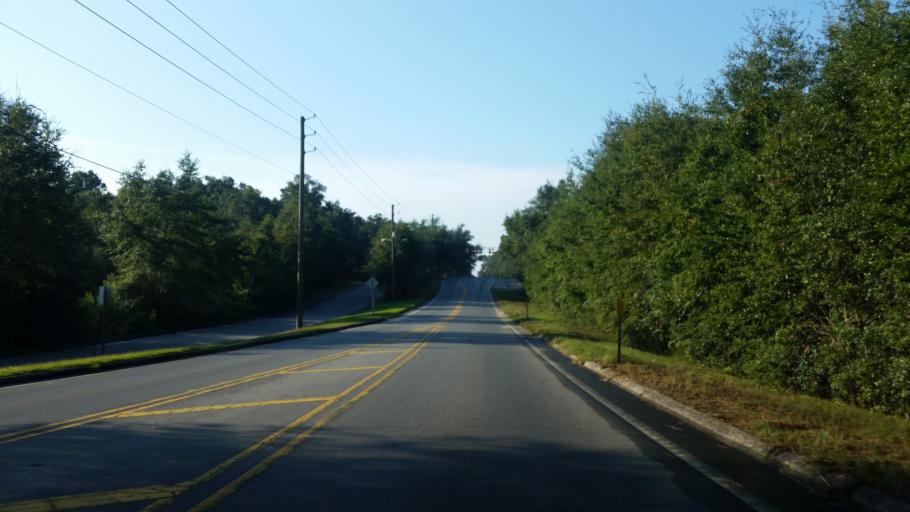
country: US
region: Florida
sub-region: Santa Rosa County
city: Milton
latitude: 30.6326
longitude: -87.0642
